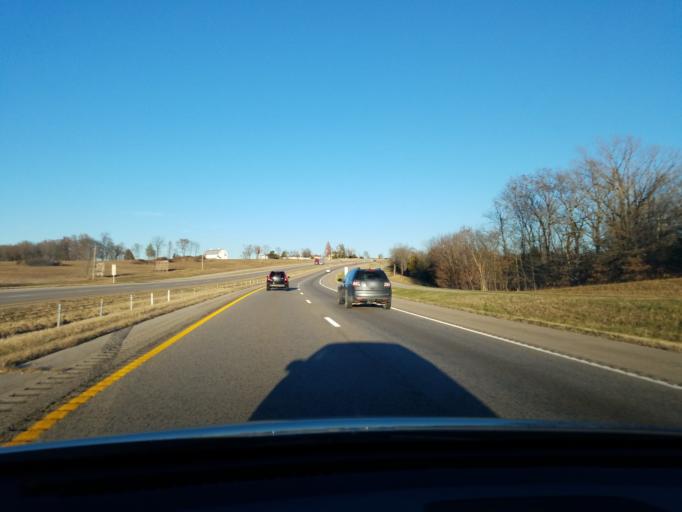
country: US
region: Missouri
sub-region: Franklin County
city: Saint Clair
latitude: 38.3946
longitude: -90.9391
